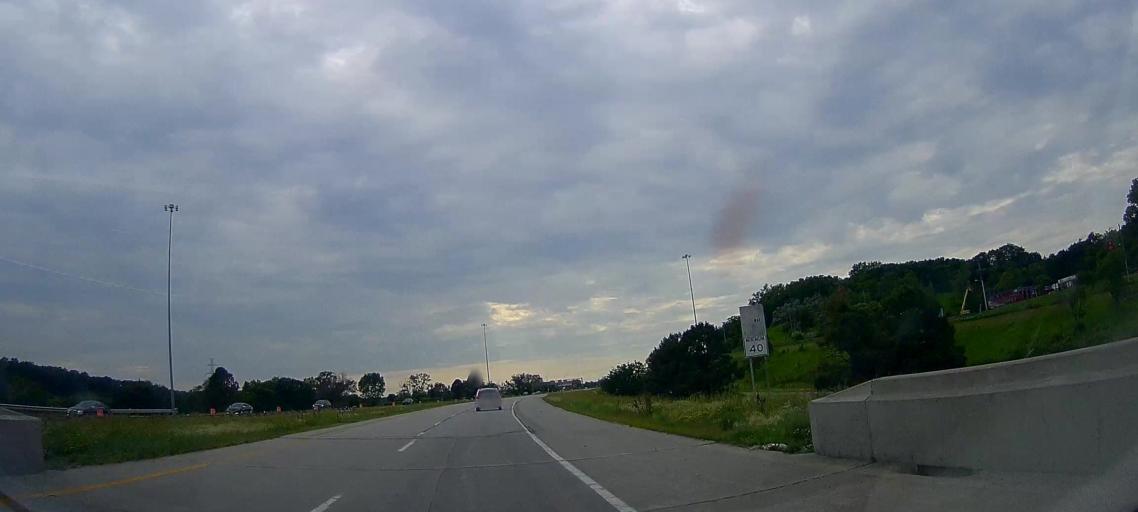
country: US
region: Iowa
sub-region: Pottawattamie County
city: Carter Lake
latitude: 41.3448
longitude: -95.9648
